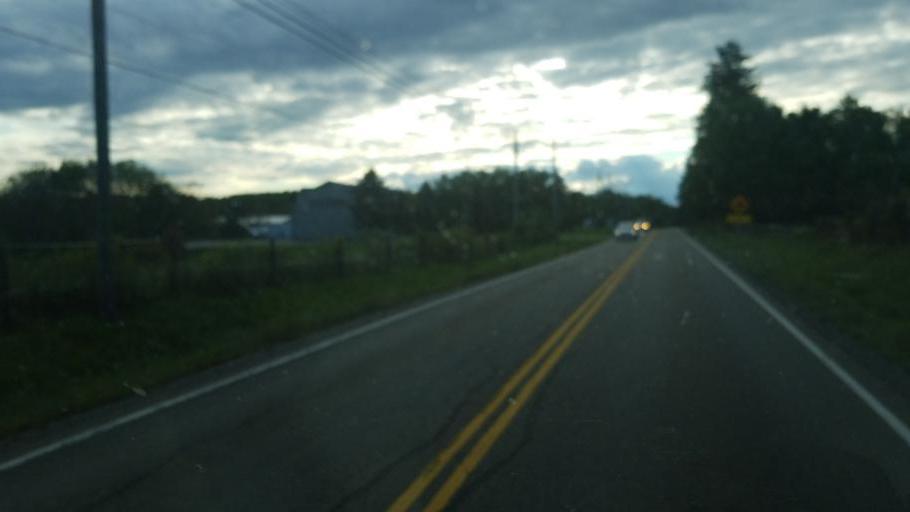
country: US
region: Ohio
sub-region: Knox County
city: Gambier
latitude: 40.4114
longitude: -82.4016
